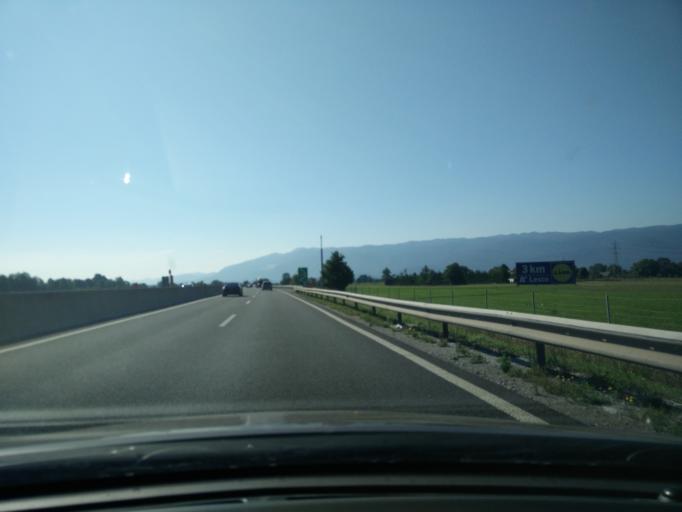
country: SI
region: Zirovnica
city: Zirovnica
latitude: 46.3968
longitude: 14.1327
